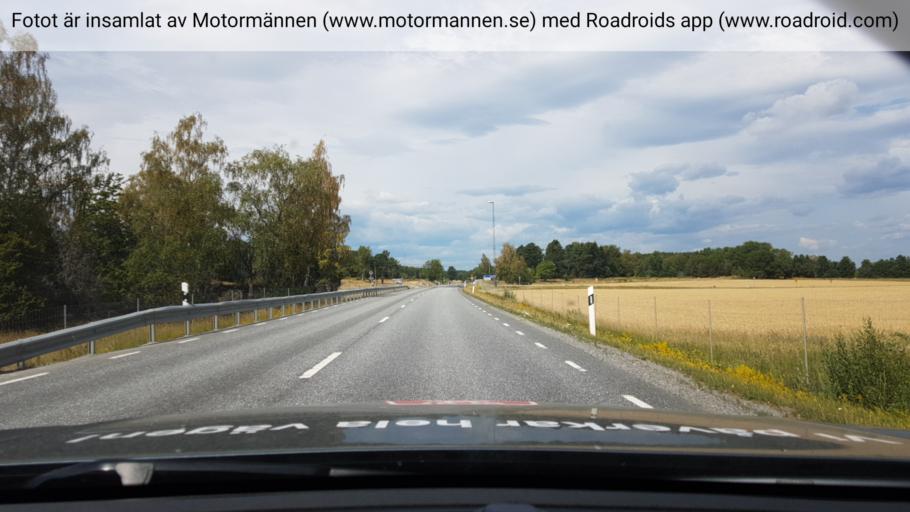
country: SE
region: Stockholm
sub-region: Upplands-Bro Kommun
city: Bro
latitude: 59.5943
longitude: 17.6160
